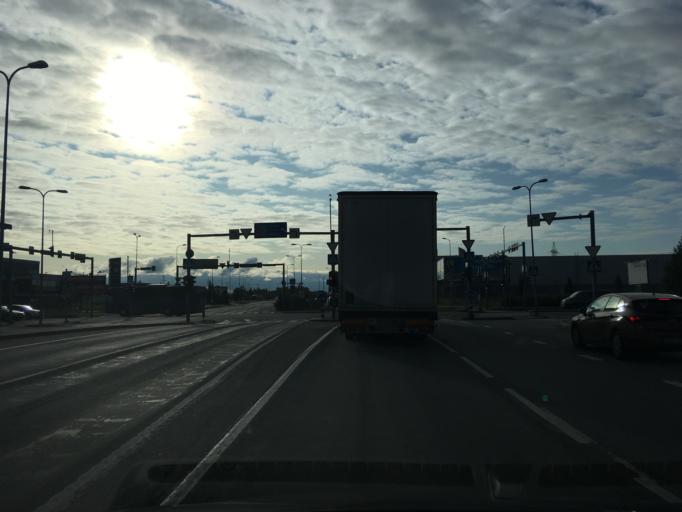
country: EE
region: Harju
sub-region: Tallinna linn
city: Kose
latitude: 59.4297
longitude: 24.8348
